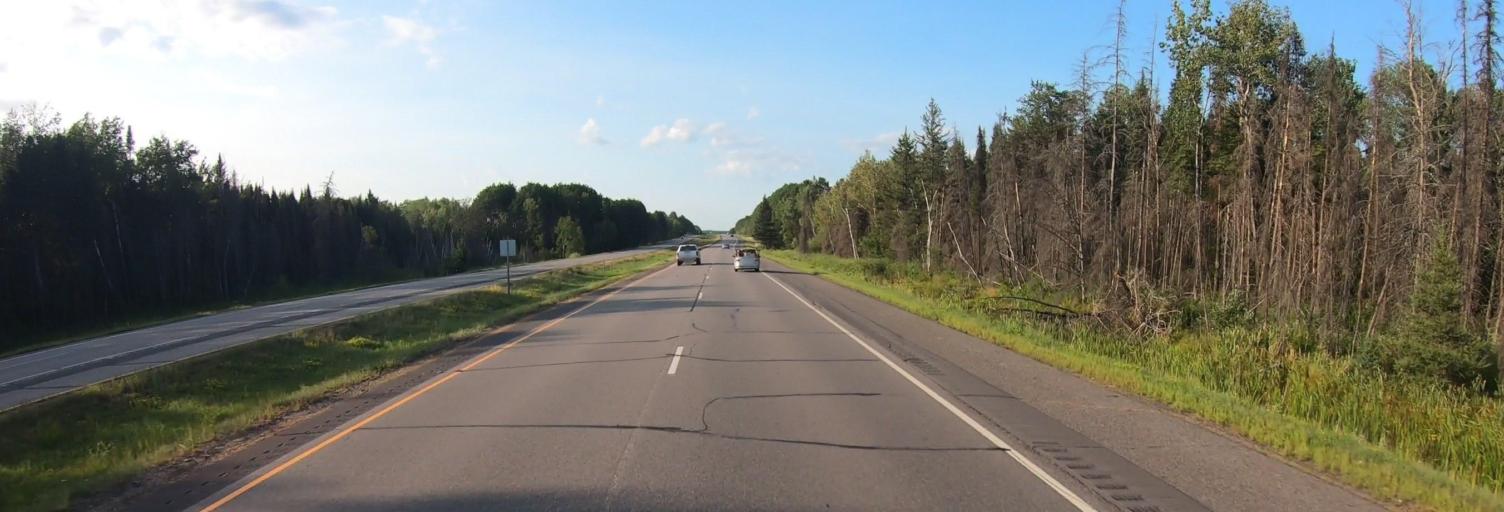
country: US
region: Minnesota
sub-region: Saint Louis County
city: Eveleth
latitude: 47.4093
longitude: -92.5207
